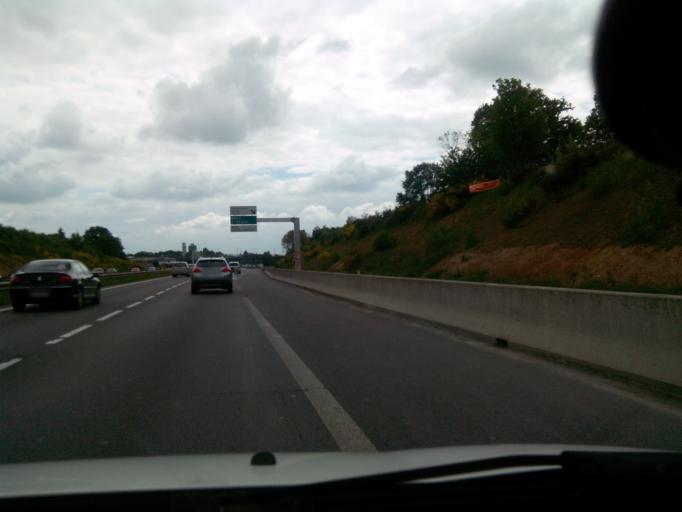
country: FR
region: Brittany
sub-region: Departement d'Ille-et-Vilaine
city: Montgermont
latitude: 48.1316
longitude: -1.7092
